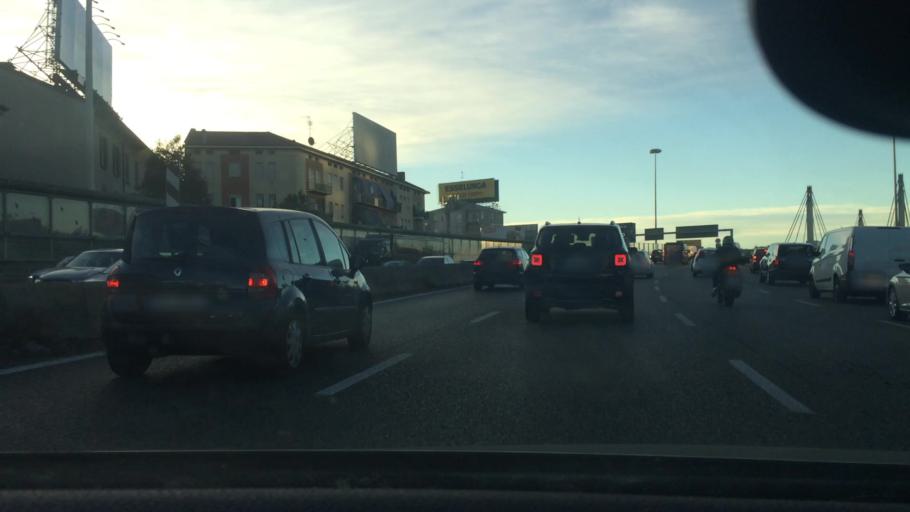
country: IT
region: Lombardy
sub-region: Citta metropolitana di Milano
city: Baranzate
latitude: 45.5103
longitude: 9.1291
